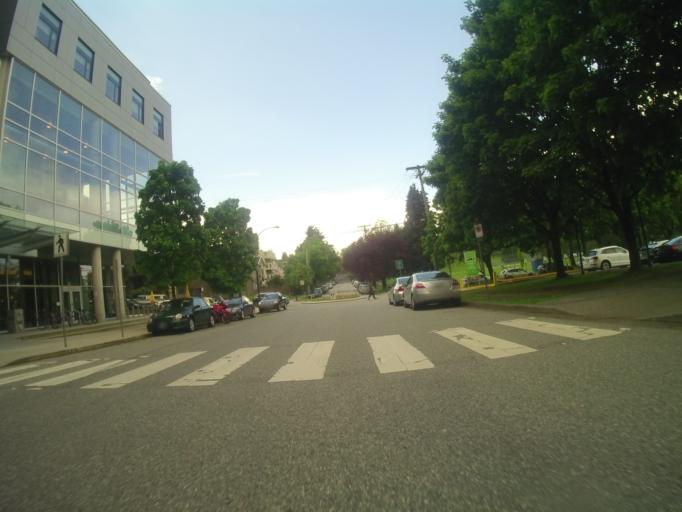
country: CA
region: British Columbia
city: Vancouver
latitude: 49.2643
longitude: -123.0805
